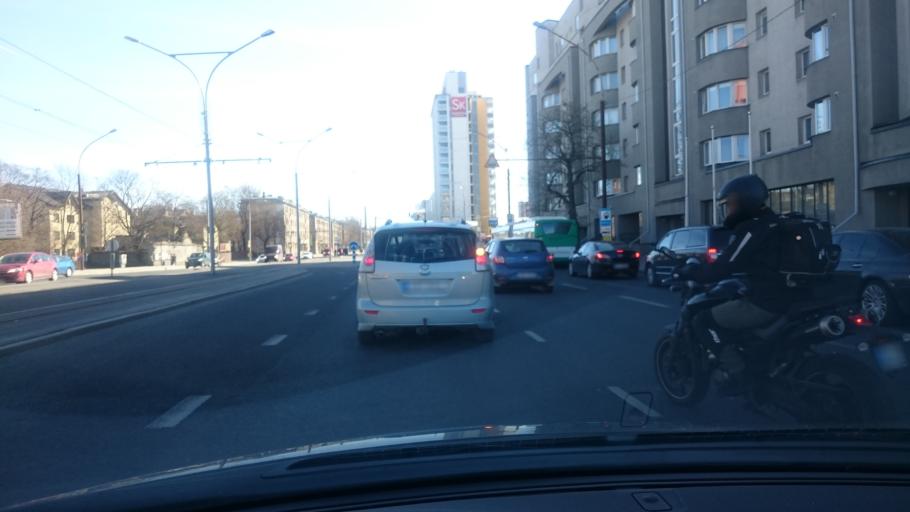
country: EE
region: Harju
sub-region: Tallinna linn
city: Tallinn
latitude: 59.4160
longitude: 24.7398
